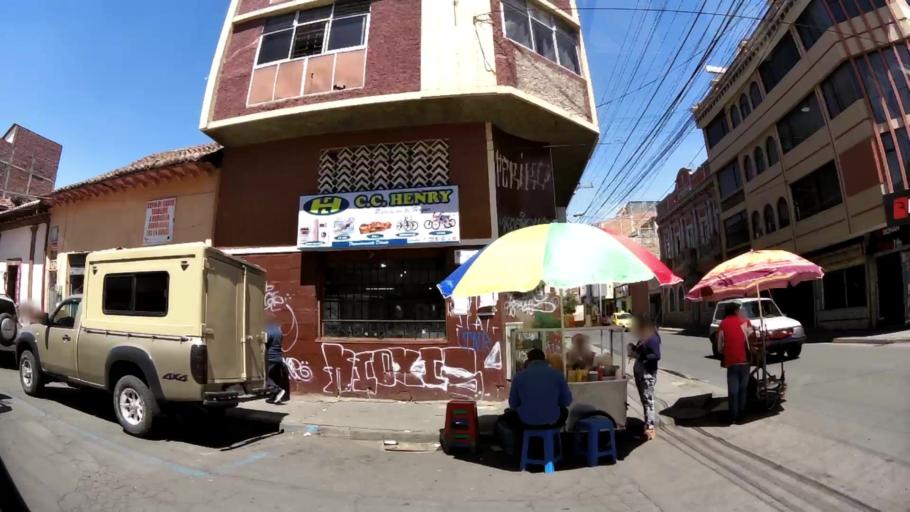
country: EC
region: Chimborazo
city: Riobamba
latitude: -1.6721
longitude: -78.6531
